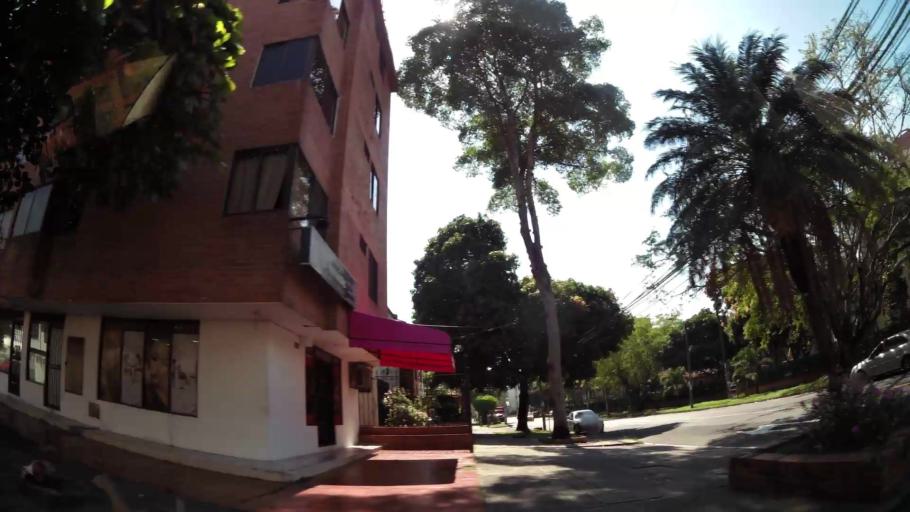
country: CO
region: Valle del Cauca
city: Cali
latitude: 3.4260
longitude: -76.5301
